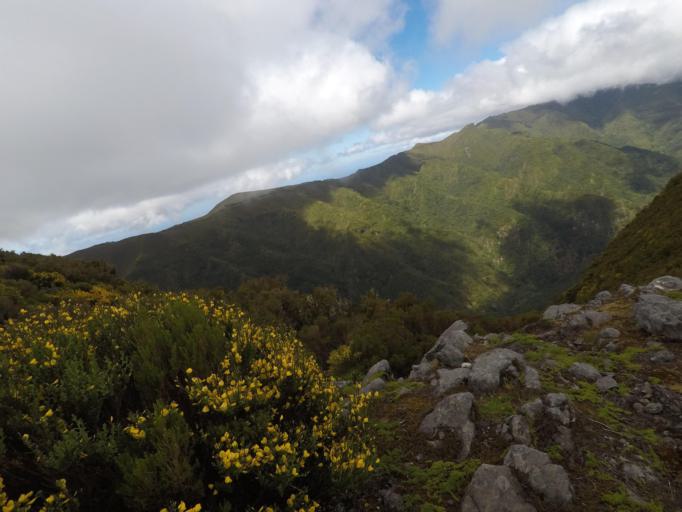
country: PT
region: Madeira
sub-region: Calheta
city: Arco da Calheta
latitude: 32.7741
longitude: -17.1326
